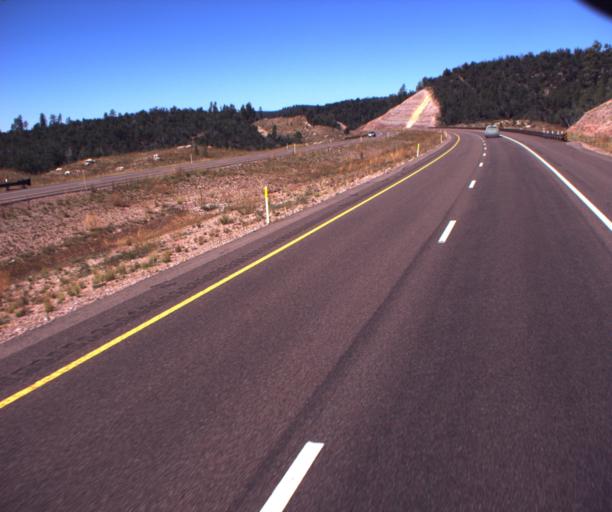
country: US
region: Arizona
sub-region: Gila County
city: Star Valley
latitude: 34.3206
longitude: -111.0654
